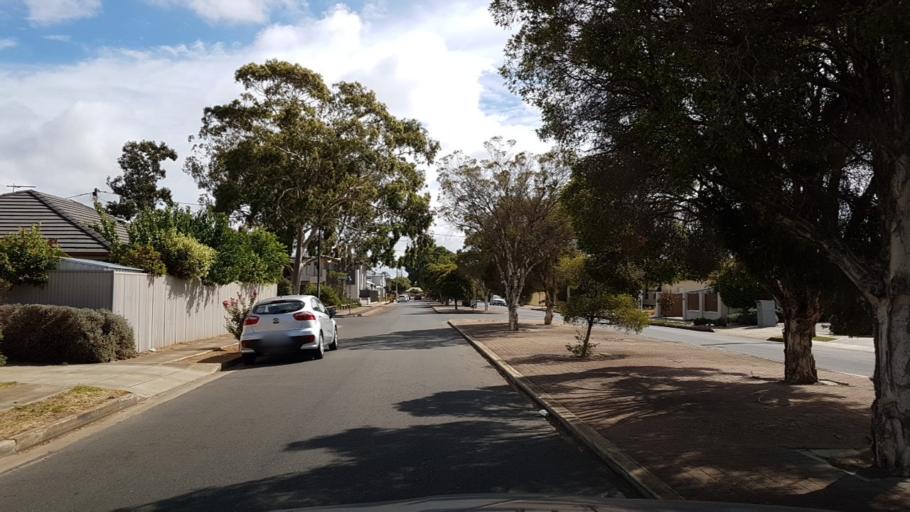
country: AU
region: South Australia
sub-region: Marion
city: Plympton Park
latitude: -34.9937
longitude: 138.5513
